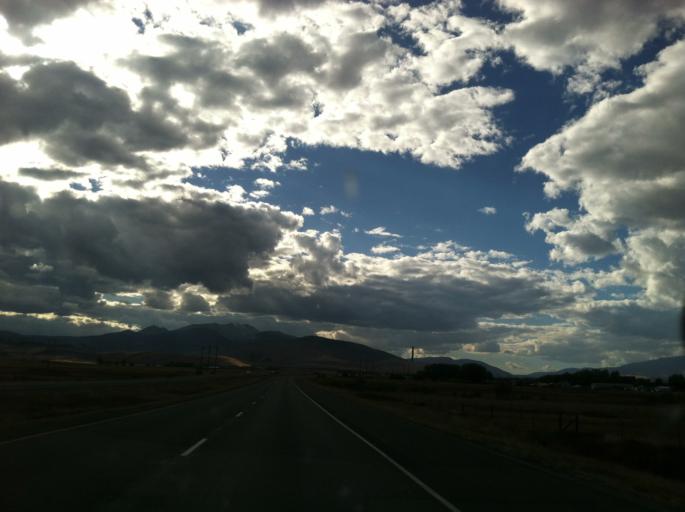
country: US
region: Montana
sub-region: Deer Lodge County
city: Warm Springs
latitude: 46.0958
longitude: -112.8186
